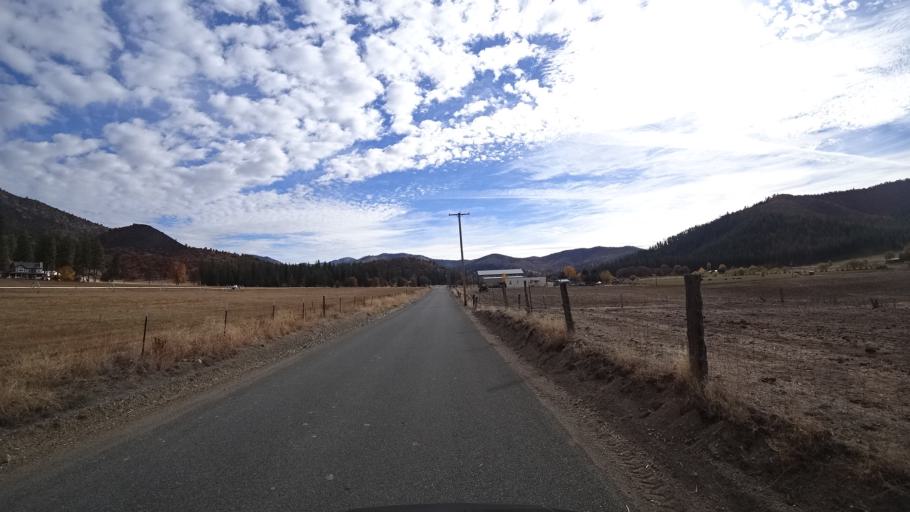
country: US
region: California
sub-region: Siskiyou County
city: Yreka
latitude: 41.6268
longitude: -122.8038
